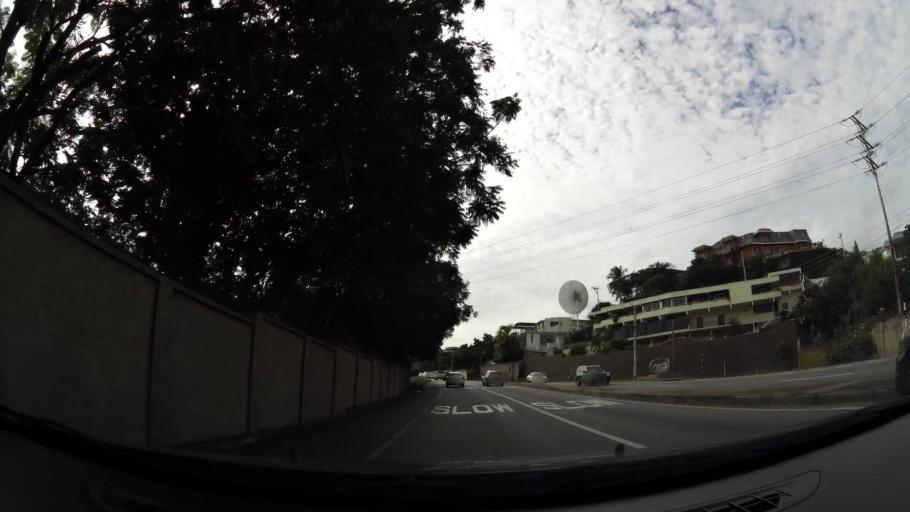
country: TT
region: City of Port of Spain
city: Mucurapo
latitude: 10.6821
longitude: -61.5630
